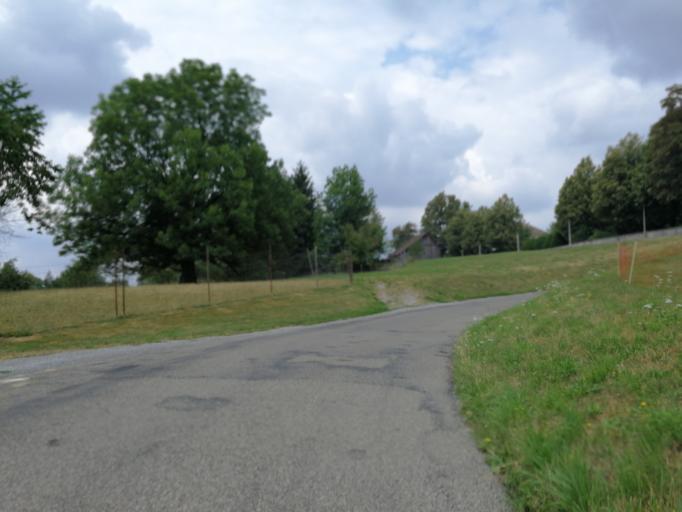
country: CH
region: Zurich
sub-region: Bezirk Hinwil
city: Binzikon
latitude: 47.2822
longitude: 8.7651
